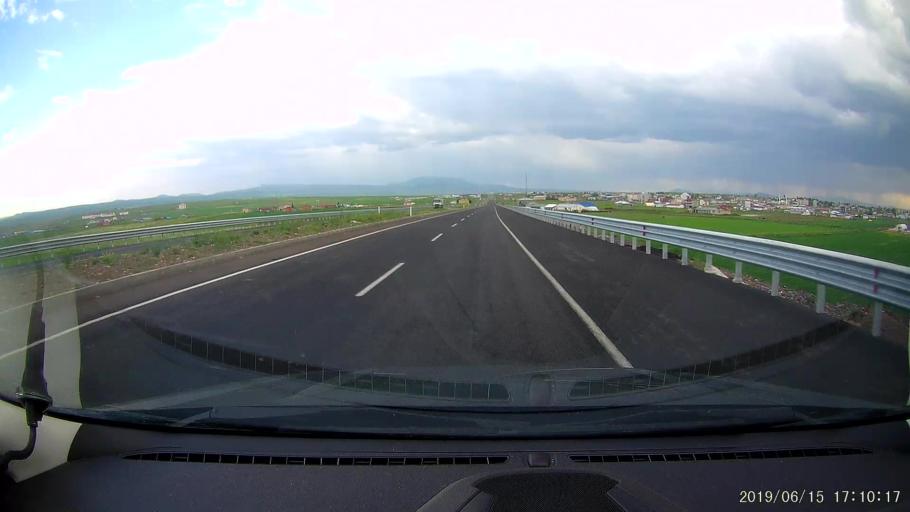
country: TR
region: Kars
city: Kars
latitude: 40.6238
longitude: 43.1338
